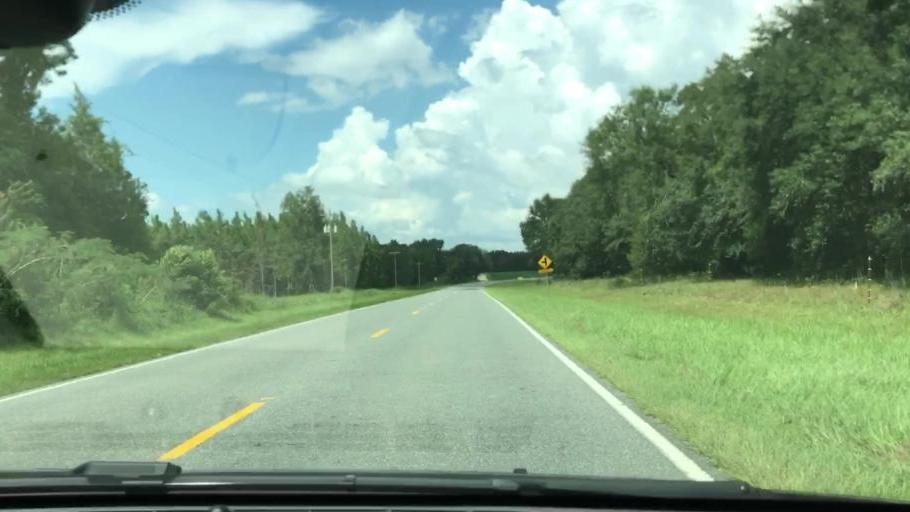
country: US
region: Florida
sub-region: Jackson County
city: Malone
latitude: 30.9555
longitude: -85.1181
